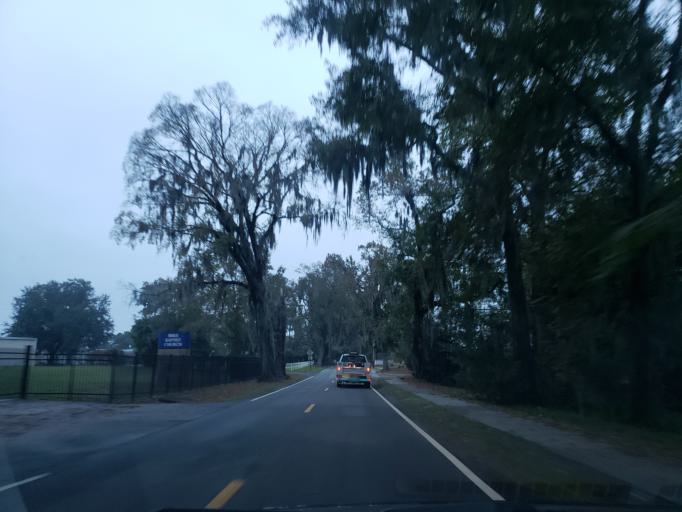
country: US
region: Georgia
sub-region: Chatham County
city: Thunderbolt
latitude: 32.0230
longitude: -81.0688
